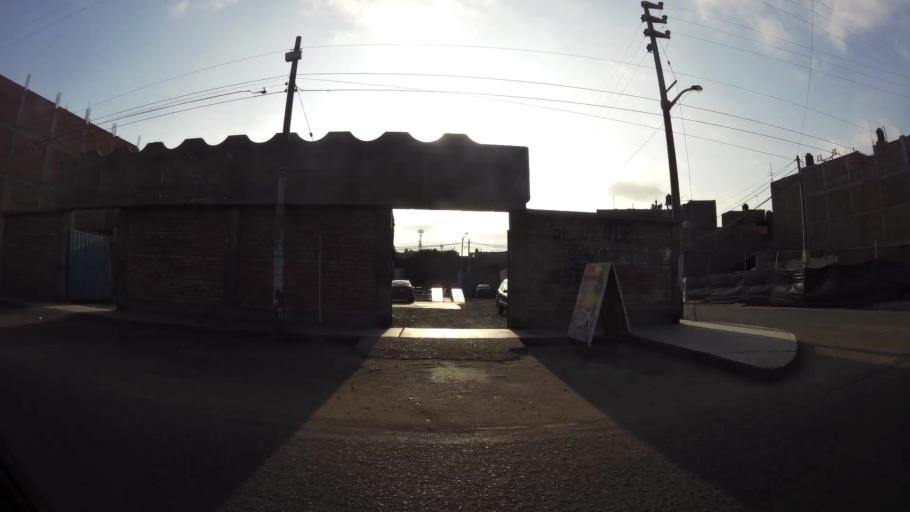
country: PE
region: La Libertad
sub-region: Provincia de Trujillo
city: El Porvenir
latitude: -8.0897
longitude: -79.0030
